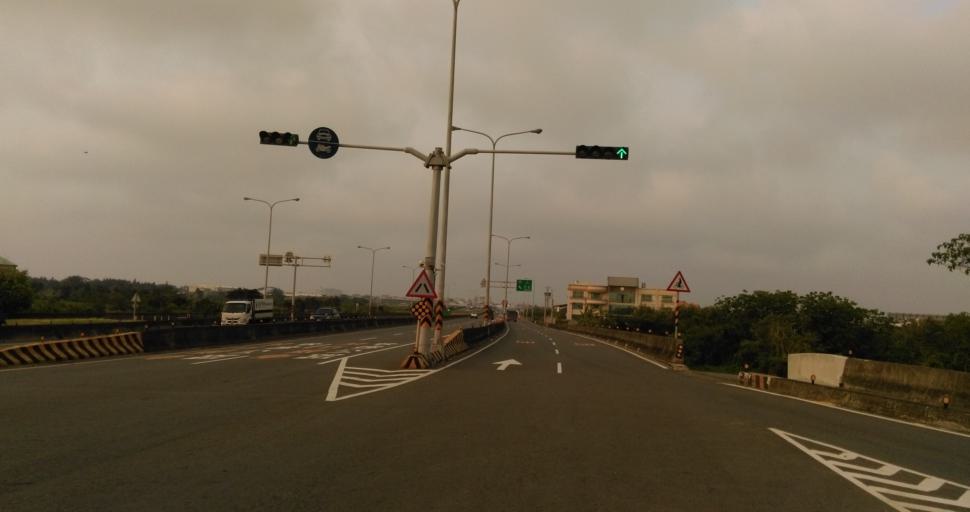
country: TW
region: Taiwan
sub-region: Hsinchu
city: Hsinchu
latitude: 24.7939
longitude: 120.9196
